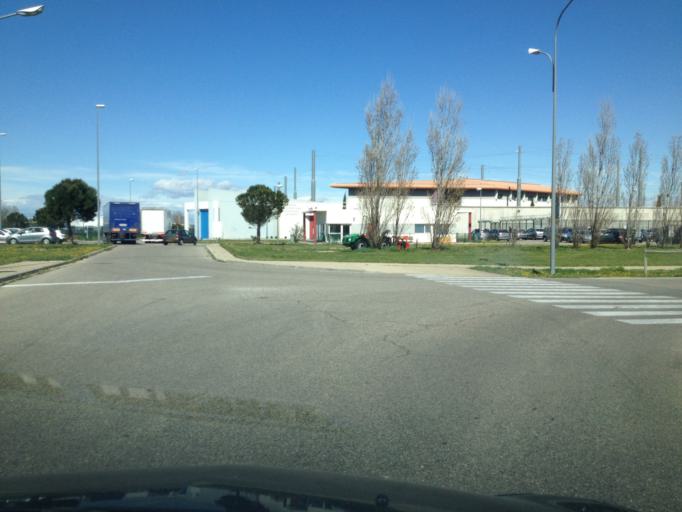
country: FR
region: Provence-Alpes-Cote d'Azur
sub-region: Departement du Vaucluse
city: Le Pontet
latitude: 43.9675
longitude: 4.8612
